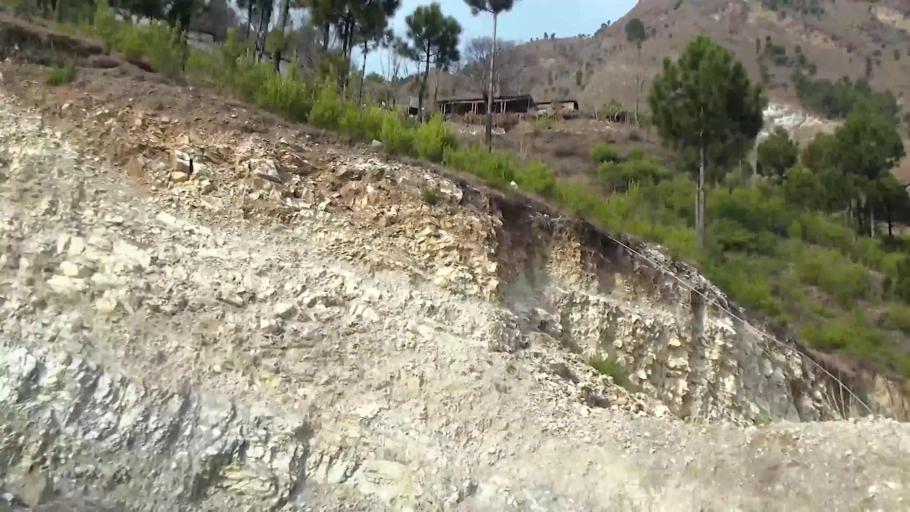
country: PK
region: Azad Kashmir
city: Muzaffarabad
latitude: 34.3623
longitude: 73.5072
